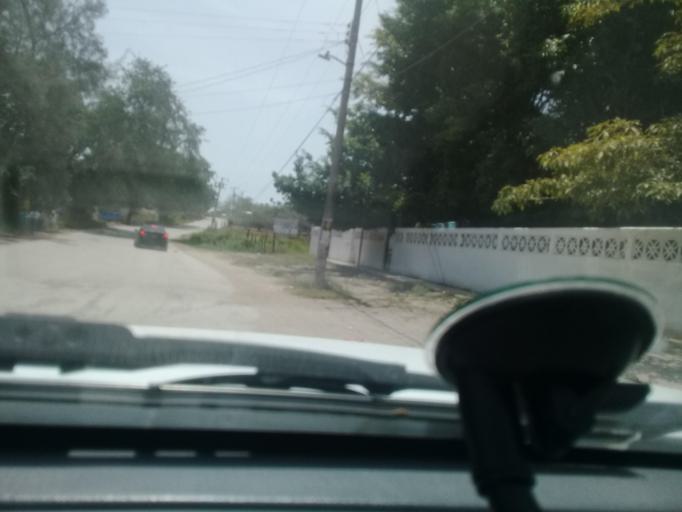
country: MX
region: Veracruz
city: Anahuac
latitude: 22.2288
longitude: -97.8263
